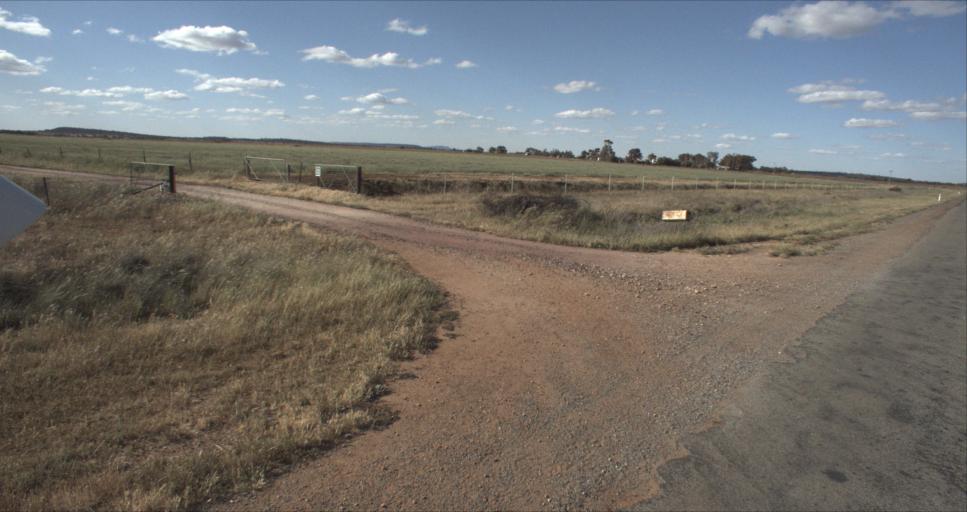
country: AU
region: New South Wales
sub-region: Leeton
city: Leeton
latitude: -34.4569
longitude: 146.2722
